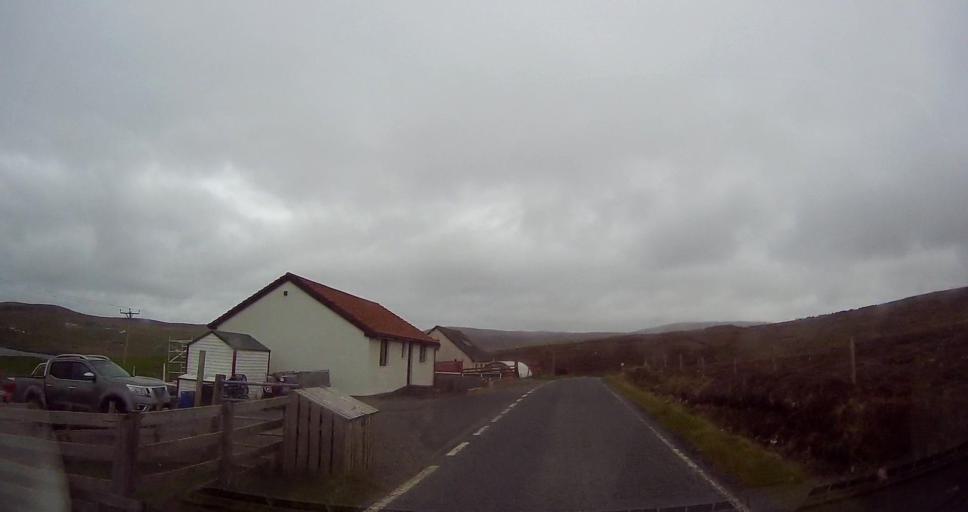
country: GB
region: Scotland
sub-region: Shetland Islands
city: Lerwick
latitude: 60.2972
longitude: -1.3629
